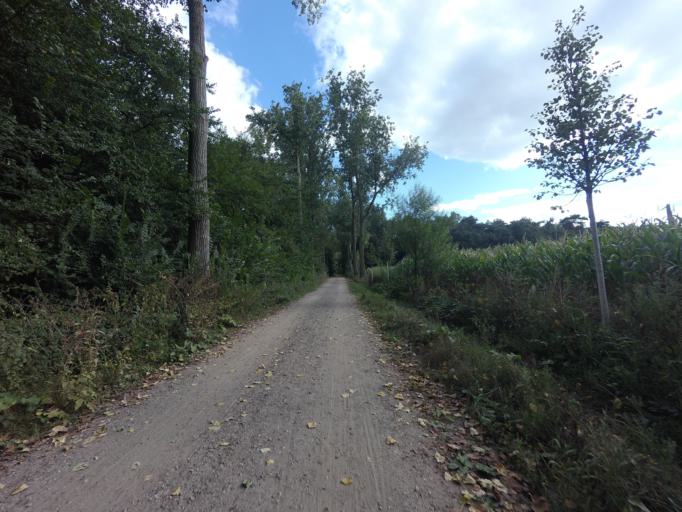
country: NL
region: North Brabant
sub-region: Gemeente Grave
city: Grave
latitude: 51.7344
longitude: 5.7417
